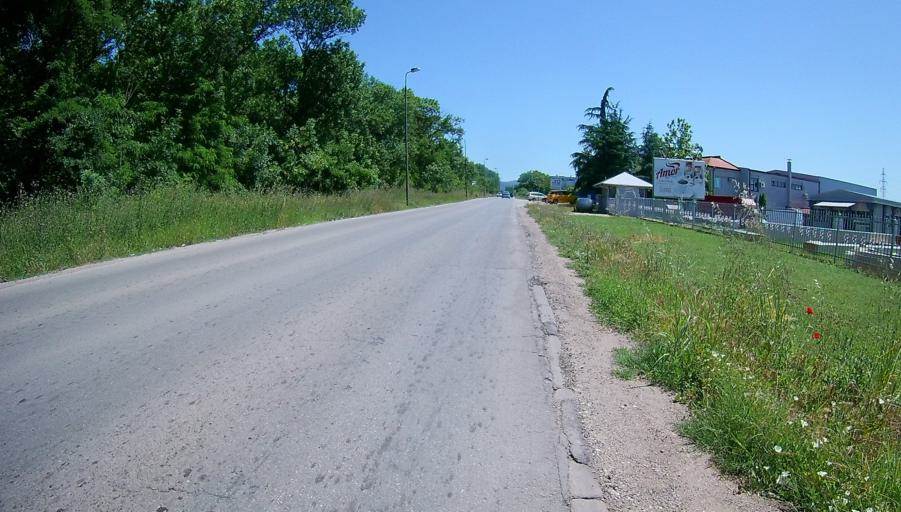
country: RS
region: Central Serbia
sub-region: Nisavski Okrug
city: Nis
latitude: 43.3009
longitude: 21.8740
